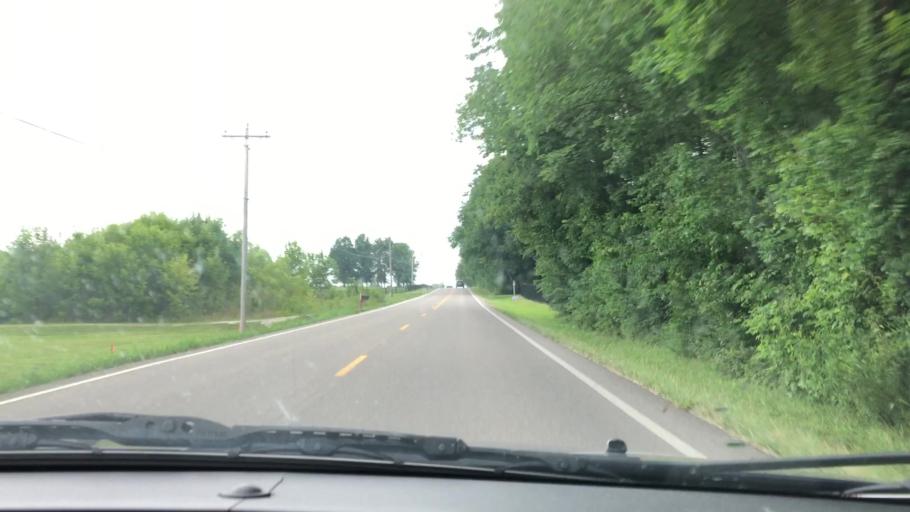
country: US
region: Tennessee
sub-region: Maury County
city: Spring Hill
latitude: 35.7447
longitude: -87.0095
